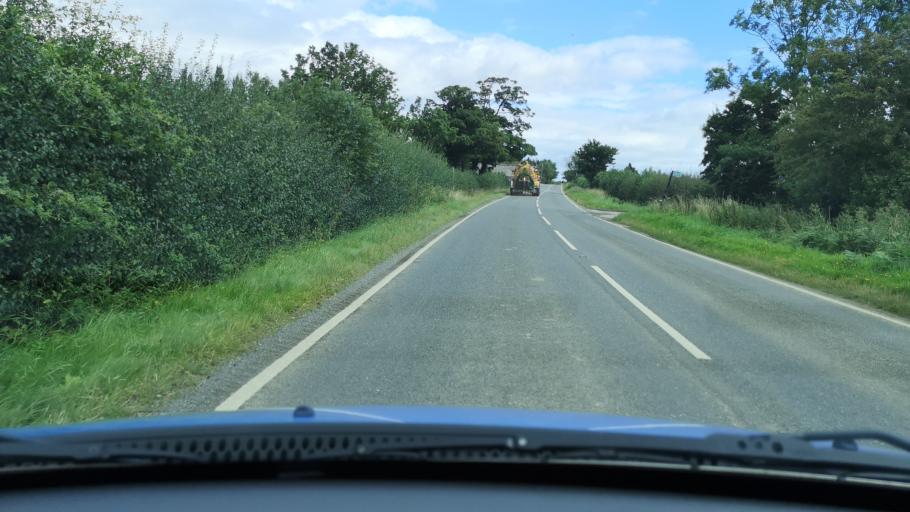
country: GB
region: England
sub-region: City and Borough of Wakefield
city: Badsworth
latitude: 53.6202
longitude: -1.3271
